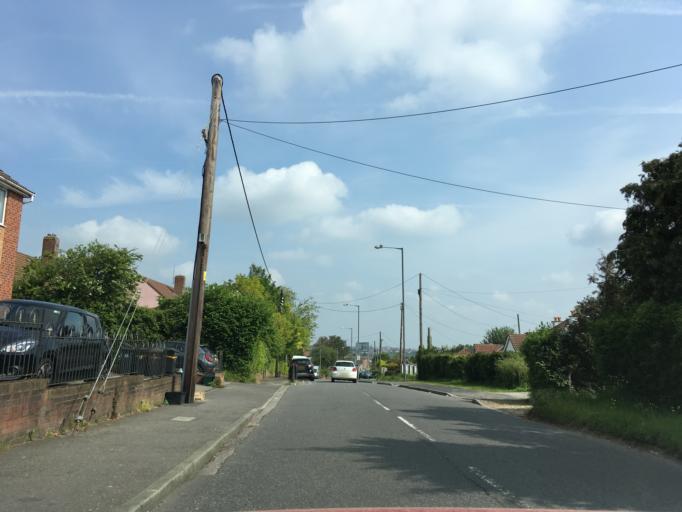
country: GB
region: England
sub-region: North Somerset
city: Dundry
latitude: 51.4055
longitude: -2.6224
